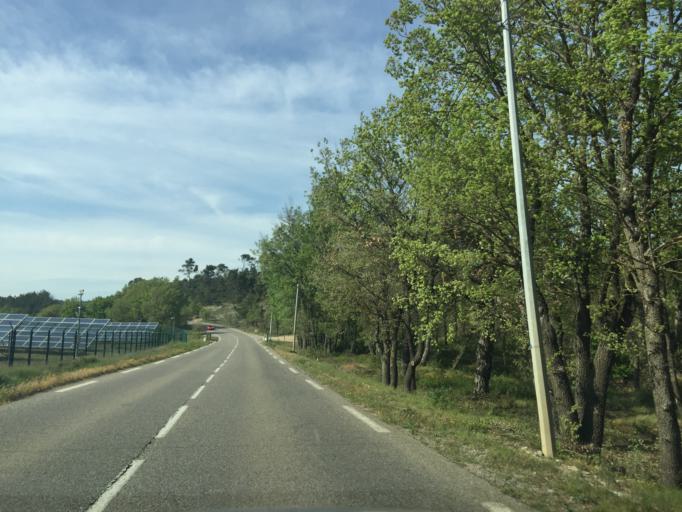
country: FR
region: Provence-Alpes-Cote d'Azur
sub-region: Departement du Var
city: Ginasservis
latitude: 43.6922
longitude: 5.8361
